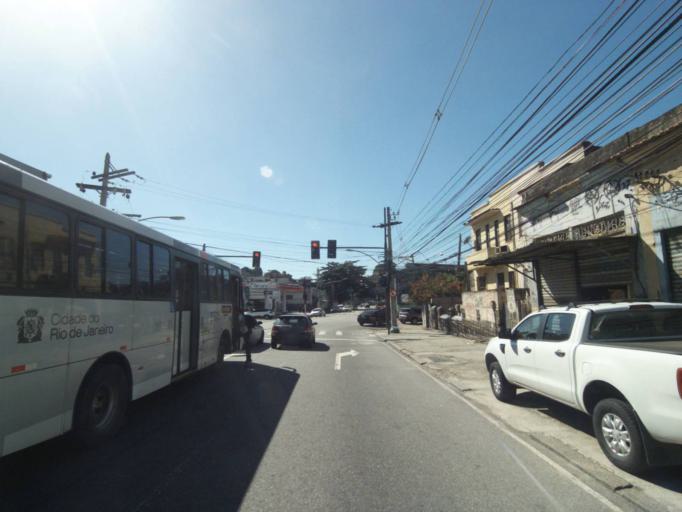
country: BR
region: Rio de Janeiro
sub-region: Rio De Janeiro
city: Rio de Janeiro
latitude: -22.9023
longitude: -43.2694
